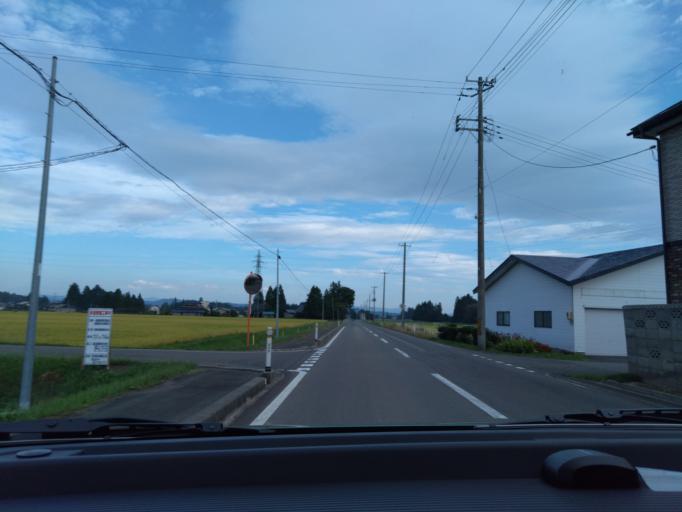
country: JP
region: Iwate
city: Kitakami
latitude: 39.3291
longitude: 141.0569
